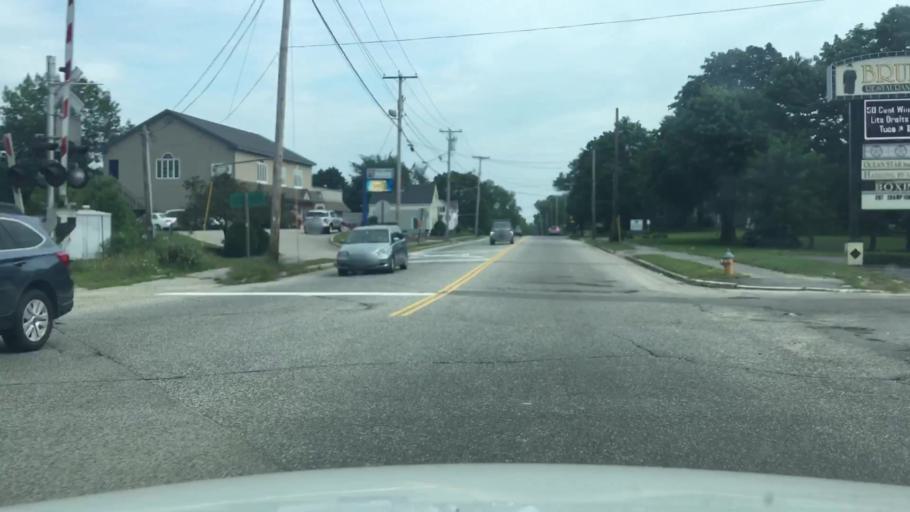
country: US
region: Maine
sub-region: Cumberland County
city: Portland
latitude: 43.6896
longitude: -70.2935
